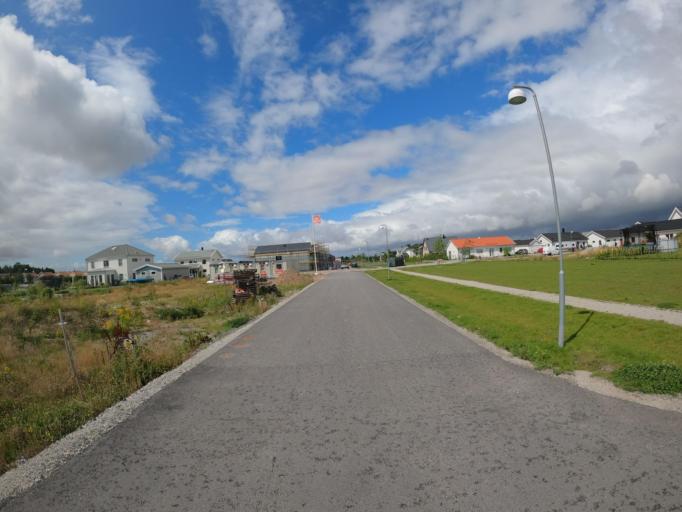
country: SE
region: Skane
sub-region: Lunds Kommun
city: Genarp
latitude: 55.7236
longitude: 13.3612
